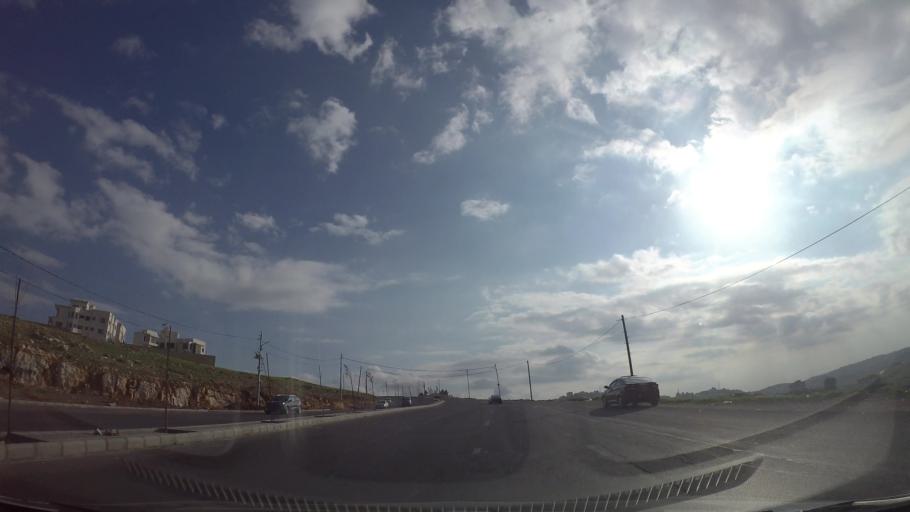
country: JO
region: Amman
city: Wadi as Sir
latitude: 31.9257
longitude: 35.8482
